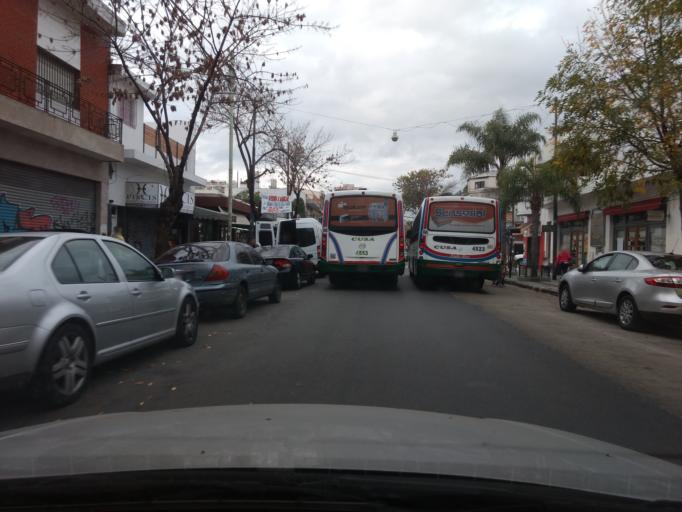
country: AR
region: Buenos Aires F.D.
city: Villa Santa Rita
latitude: -34.6227
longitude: -58.4964
